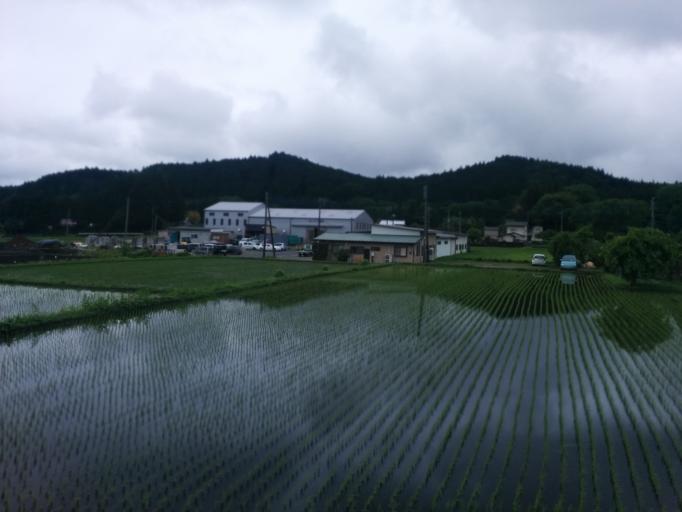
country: JP
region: Tochigi
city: Imaichi
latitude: 36.7268
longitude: 139.6699
